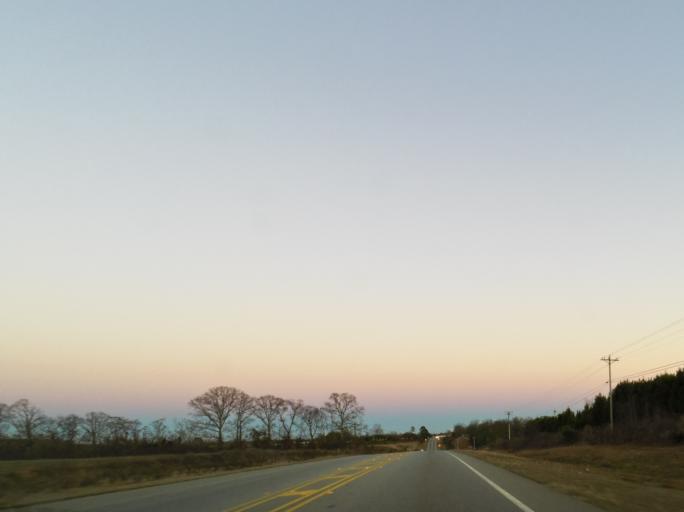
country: US
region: Georgia
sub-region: Peach County
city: Byron
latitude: 32.6066
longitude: -83.7692
